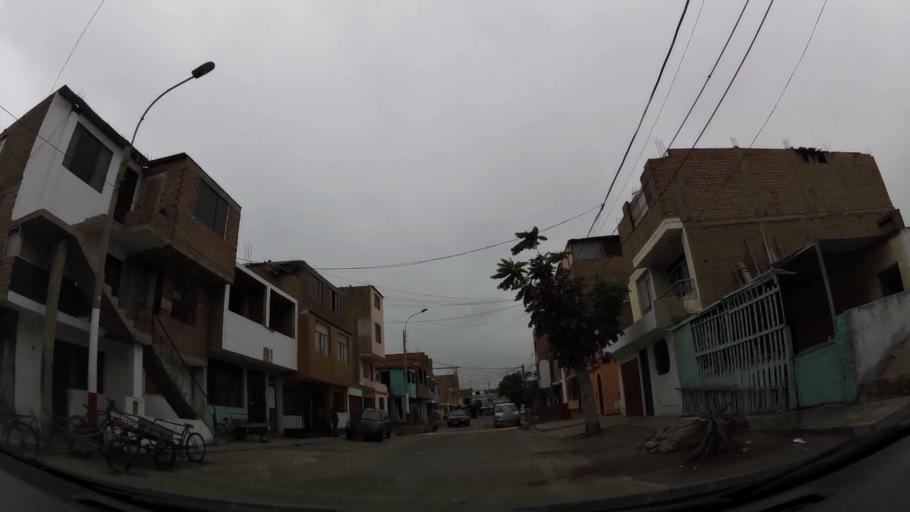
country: PE
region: Callao
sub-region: Callao
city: Callao
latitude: -12.0560
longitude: -77.1229
